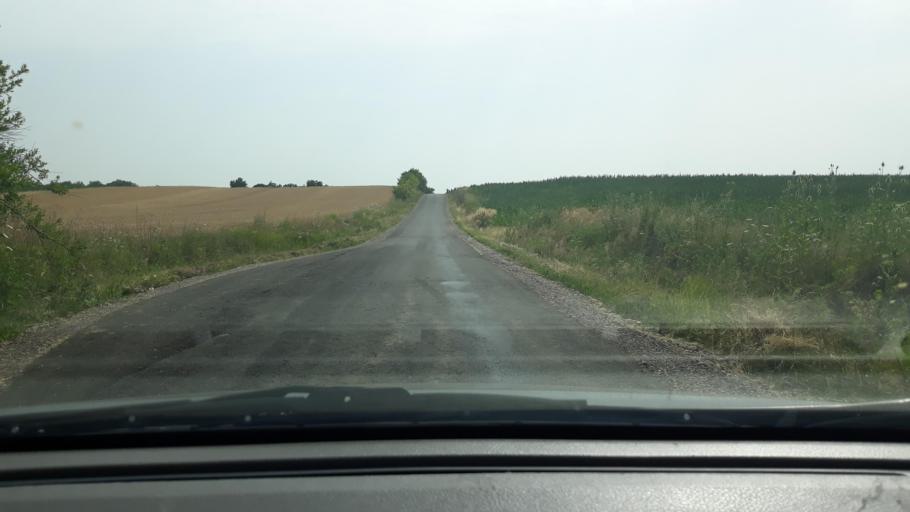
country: RO
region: Bihor
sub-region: Comuna Chislaz
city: Misca
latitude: 47.2694
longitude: 22.2643
